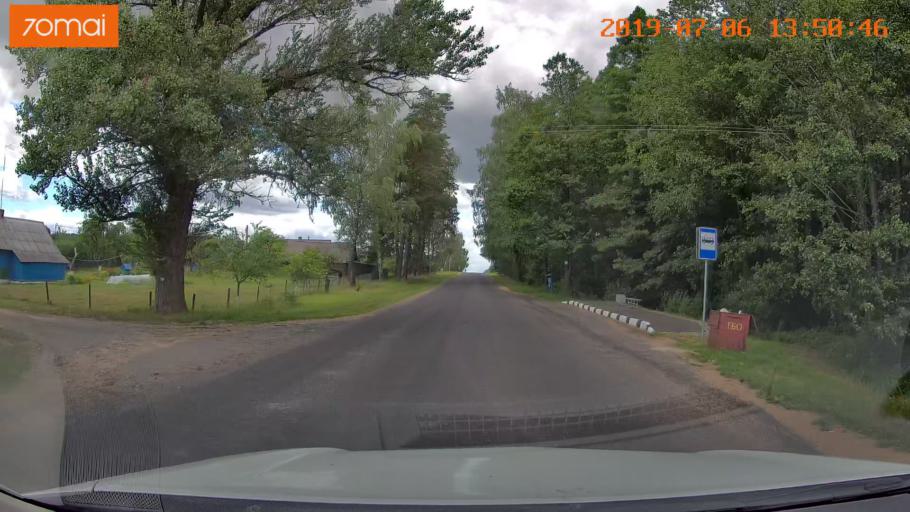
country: BY
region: Minsk
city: Ivyanyets
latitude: 53.7021
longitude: 26.8402
